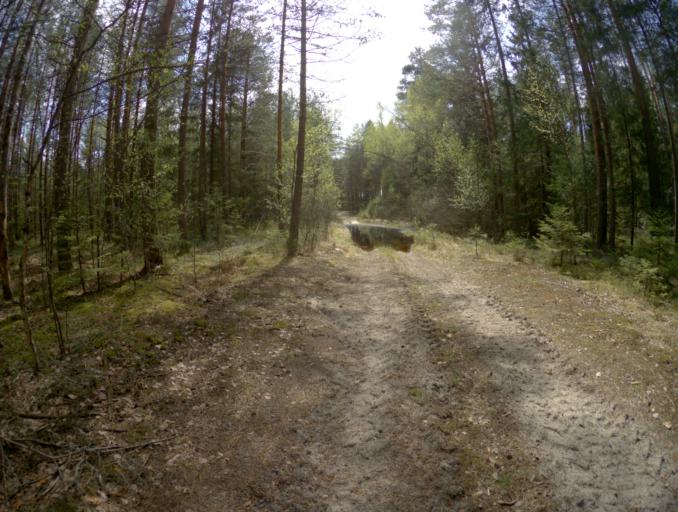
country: RU
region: Vladimir
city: Golovino
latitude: 55.8907
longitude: 40.3881
